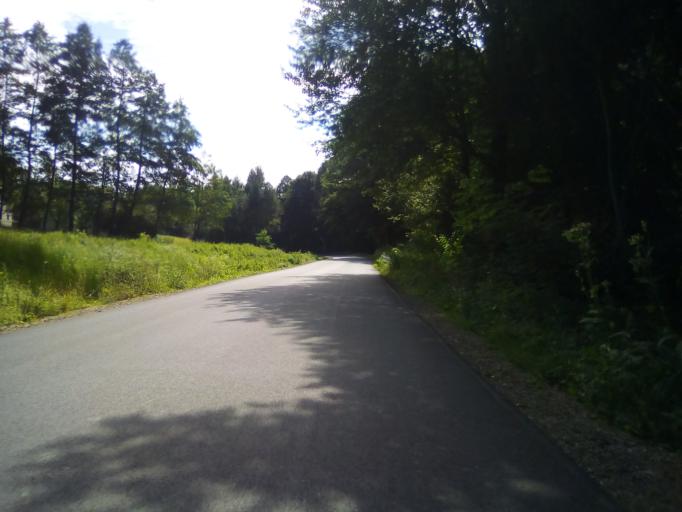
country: PL
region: Subcarpathian Voivodeship
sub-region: Powiat strzyzowski
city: Konieczkowa
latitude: 49.8156
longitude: 21.9238
